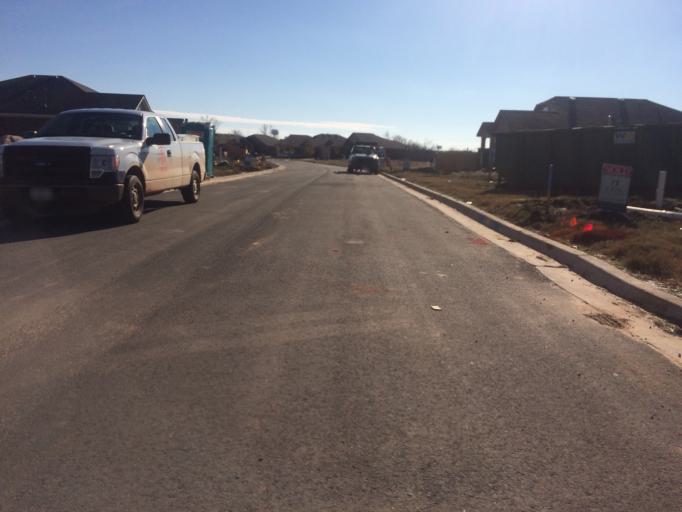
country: US
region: Oklahoma
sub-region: Cleveland County
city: Norman
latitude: 35.2535
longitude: -97.4566
